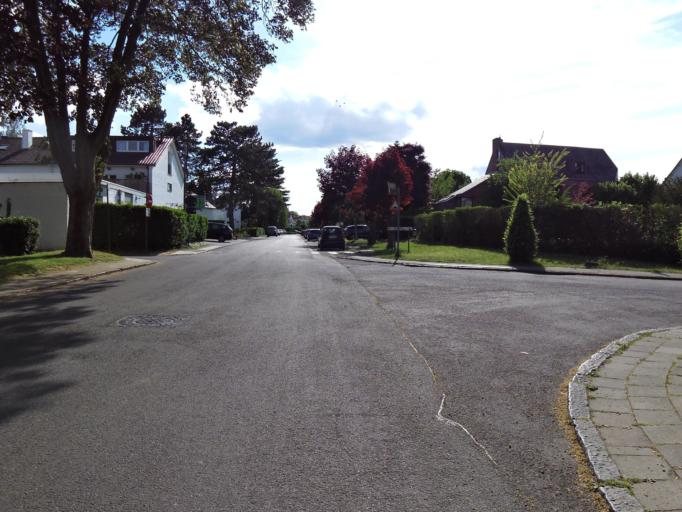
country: BE
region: Flanders
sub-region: Provincie Vlaams-Brabant
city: Wezembeek-Oppem
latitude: 50.8427
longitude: 4.4820
